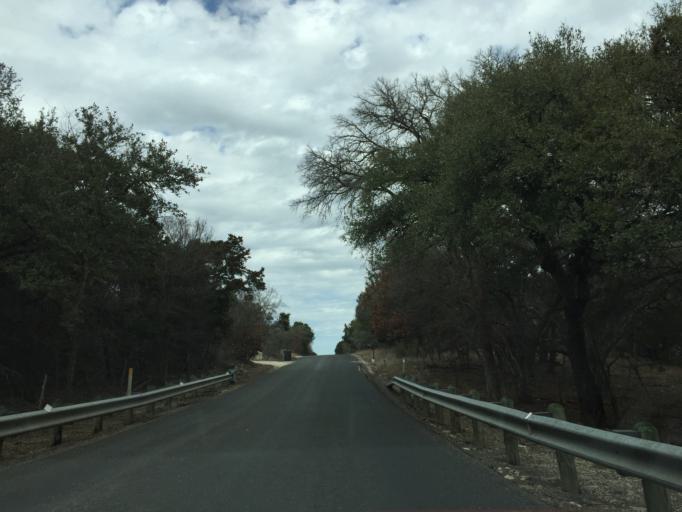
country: US
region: Texas
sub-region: Burnet County
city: Bertram
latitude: 30.7315
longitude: -97.9351
